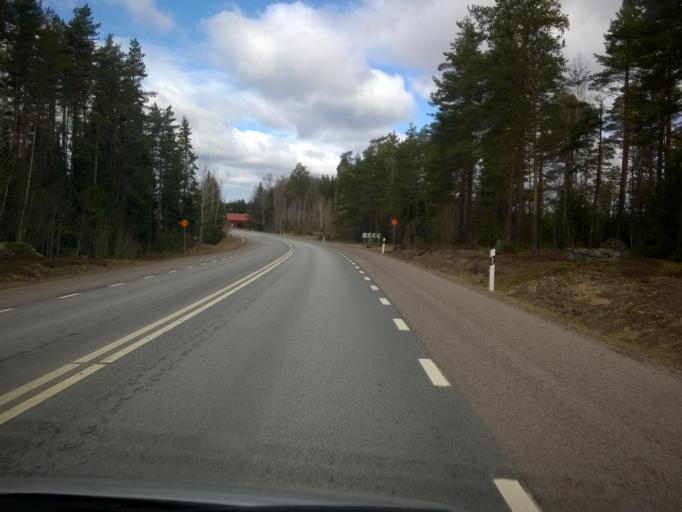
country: SE
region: Uppsala
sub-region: Tierps Kommun
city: Tierp
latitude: 60.2096
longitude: 17.4819
